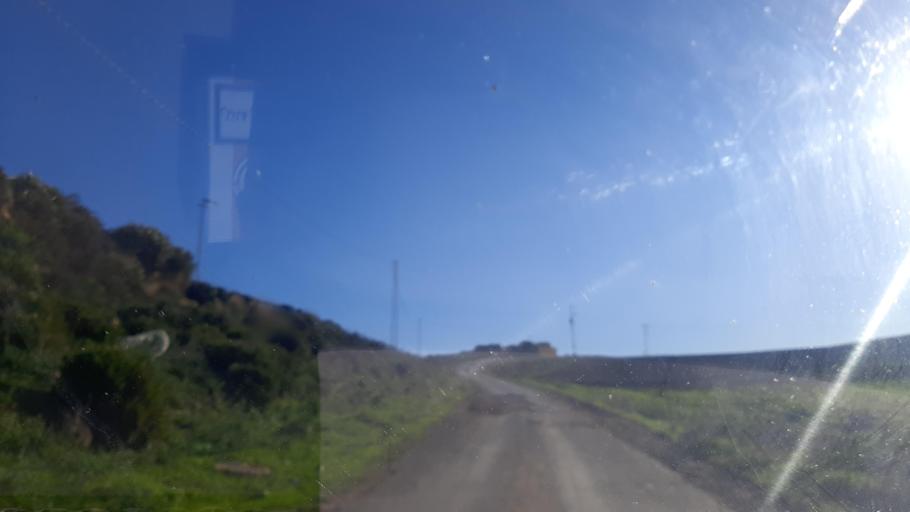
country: TN
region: Nabul
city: El Mida
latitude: 36.8091
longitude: 10.8458
